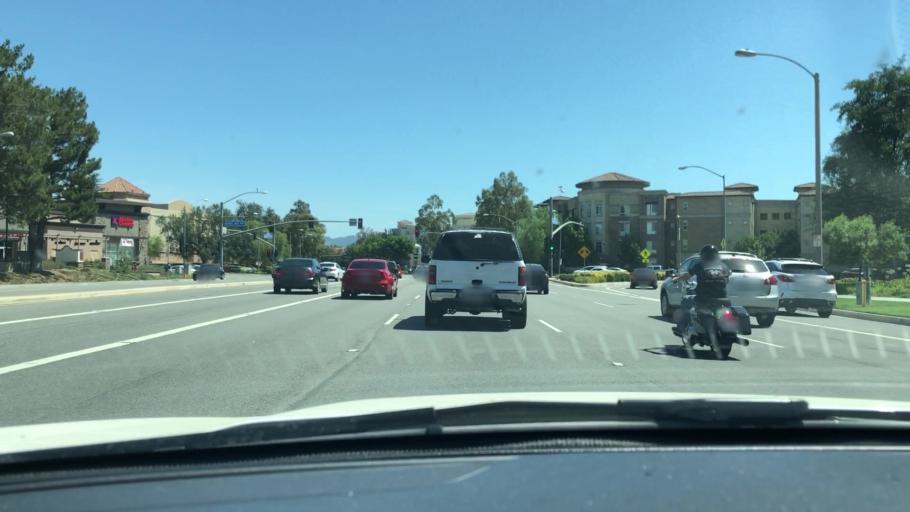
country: US
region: California
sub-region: Los Angeles County
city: Santa Clarita
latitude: 34.4209
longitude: -118.5628
